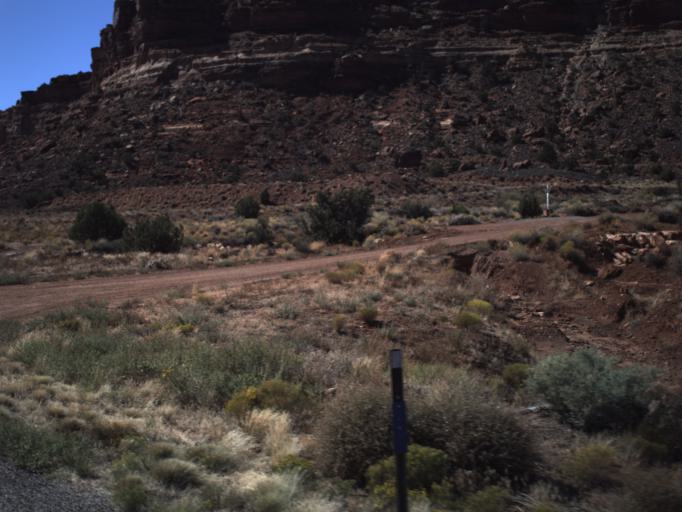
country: US
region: Utah
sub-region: San Juan County
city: Blanding
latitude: 37.7509
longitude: -110.2801
